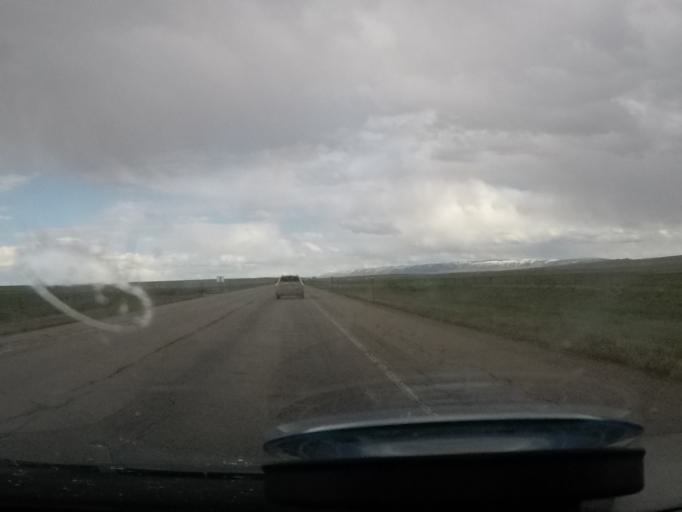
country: US
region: Wyoming
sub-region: Natrona County
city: Mills
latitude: 42.9505
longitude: -106.6339
